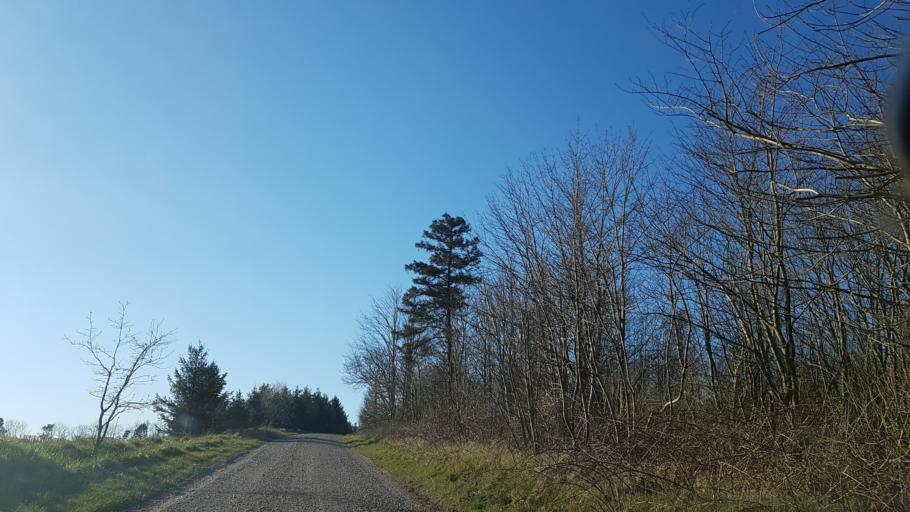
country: DK
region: South Denmark
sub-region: Vejen Kommune
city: Holsted
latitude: 55.4322
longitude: 8.9443
